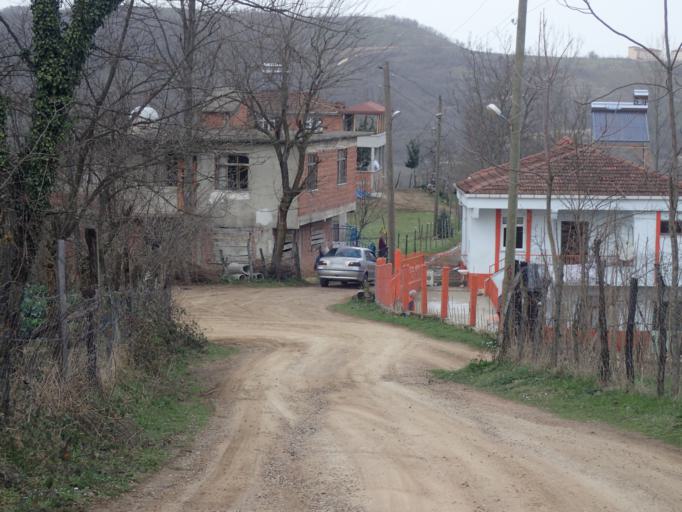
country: TR
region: Ordu
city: Camas
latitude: 40.8894
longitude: 37.4984
